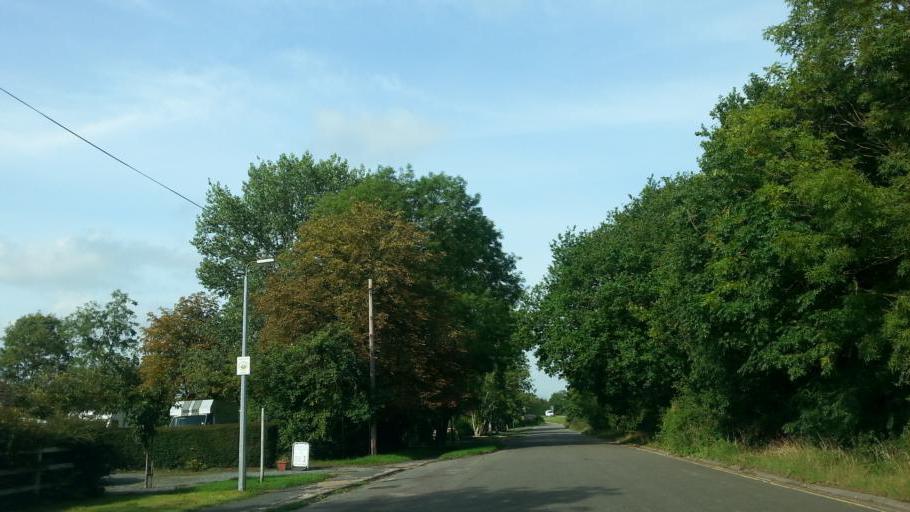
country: GB
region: England
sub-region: Cambridgeshire
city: Comberton
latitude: 52.2189
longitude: -0.0025
